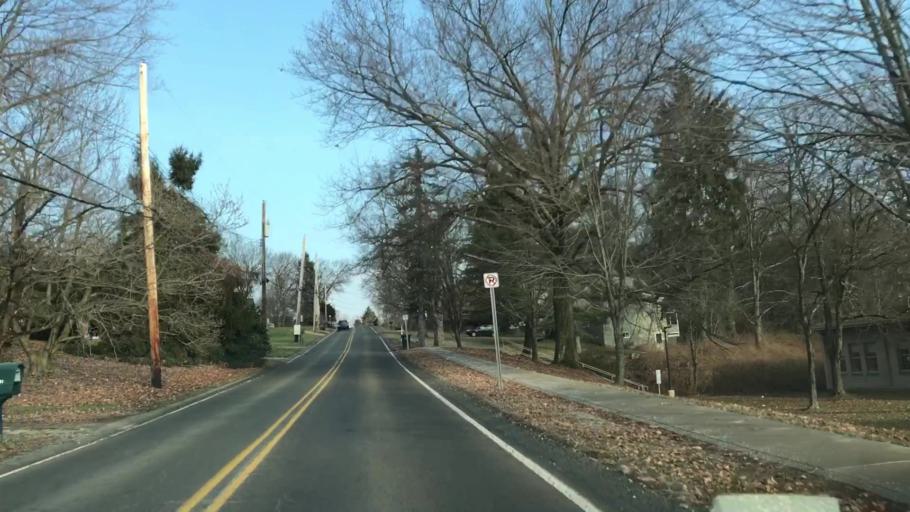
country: US
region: Pennsylvania
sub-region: Allegheny County
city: Franklin Park
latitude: 40.5822
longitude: -80.0544
